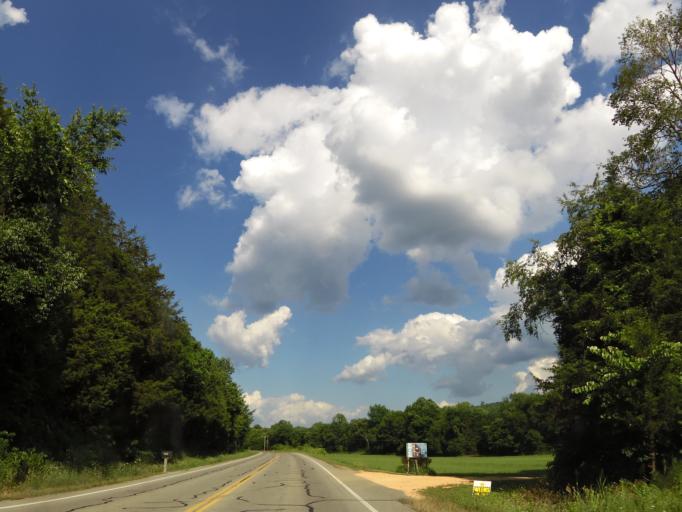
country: US
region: Tennessee
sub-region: Perry County
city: Linden
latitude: 35.6325
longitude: -87.7706
